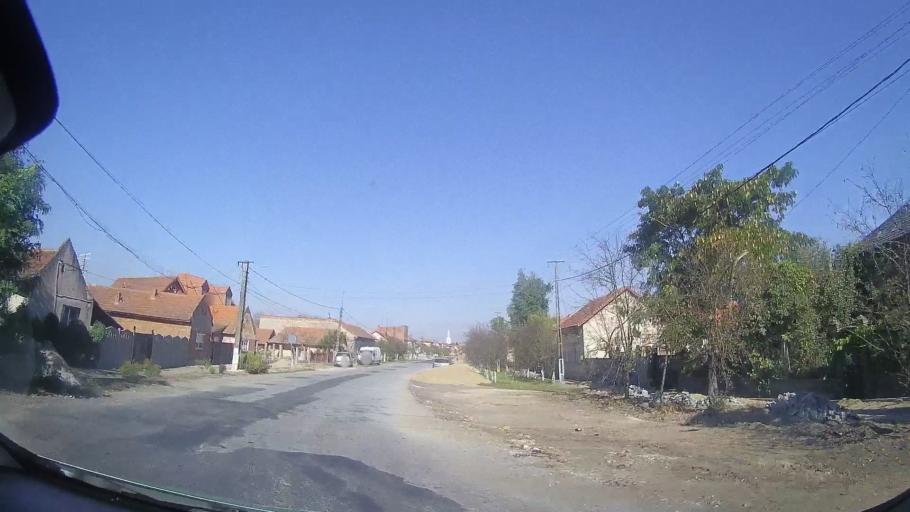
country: RO
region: Timis
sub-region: Comuna Costeiu
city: Costeiu
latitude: 45.7380
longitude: 21.8496
